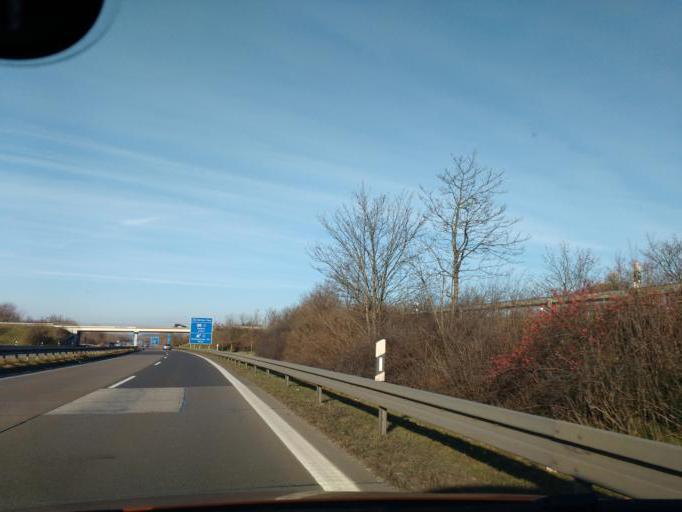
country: DE
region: Berlin
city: Buchholz
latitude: 52.6140
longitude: 13.4458
